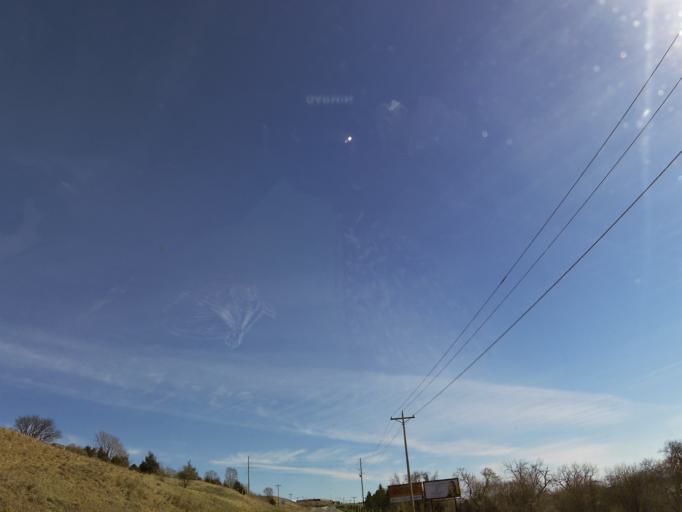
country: US
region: Minnesota
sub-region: Hennepin County
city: Eden Prairie
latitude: 44.8185
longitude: -93.4715
